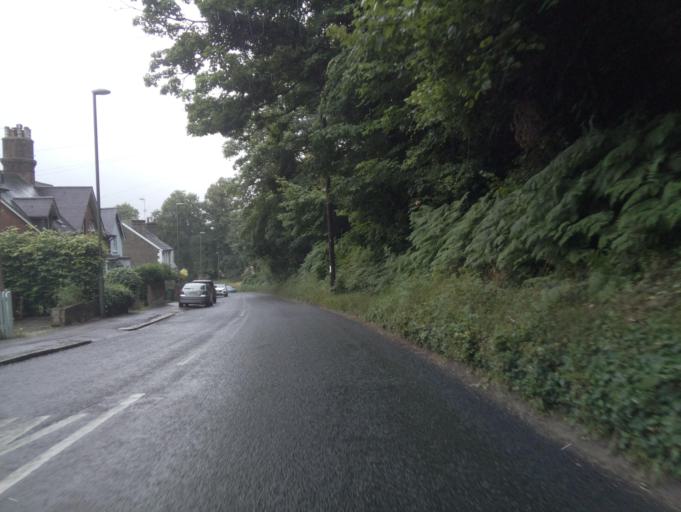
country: GB
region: England
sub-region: Surrey
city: Redhill
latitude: 51.2338
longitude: -0.1751
